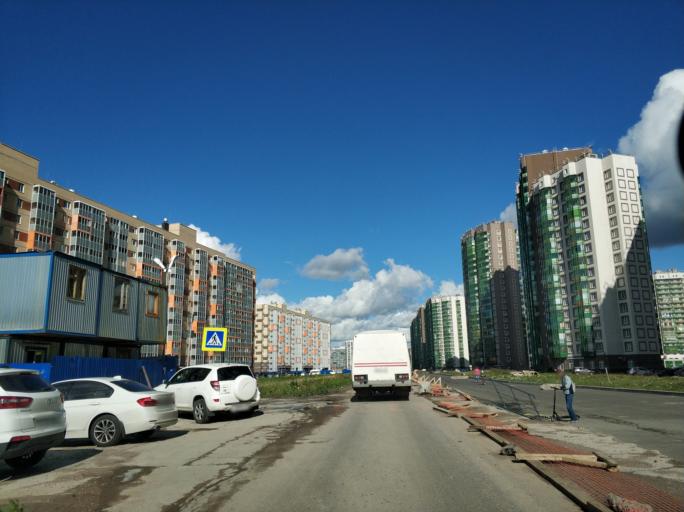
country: RU
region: St.-Petersburg
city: Grazhdanka
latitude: 60.0511
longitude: 30.4191
